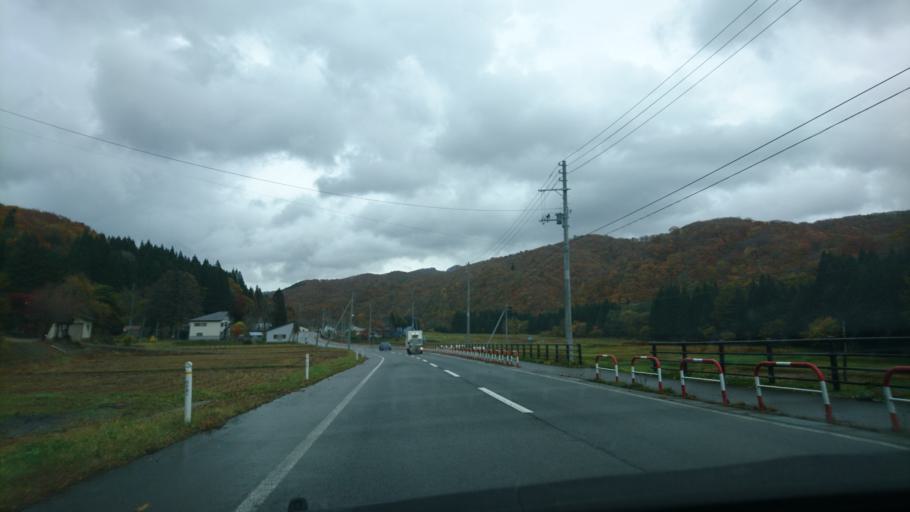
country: JP
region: Iwate
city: Shizukuishi
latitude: 39.5041
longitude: 140.8218
